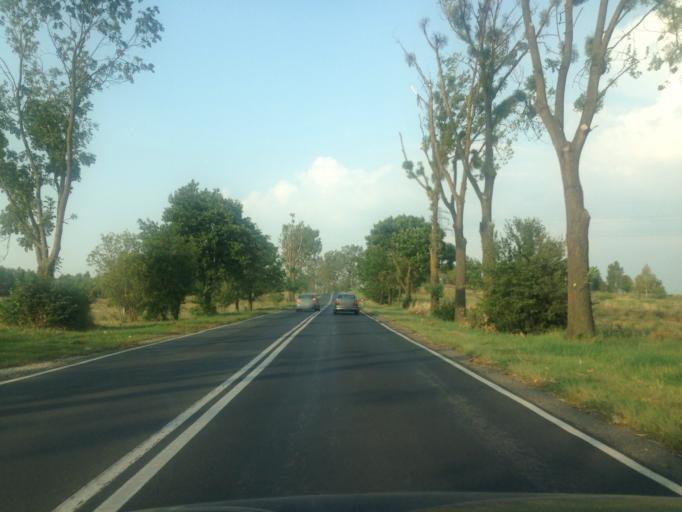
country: PL
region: Kujawsko-Pomorskie
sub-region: Powiat wloclawski
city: Fabianki
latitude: 52.7916
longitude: 19.1205
